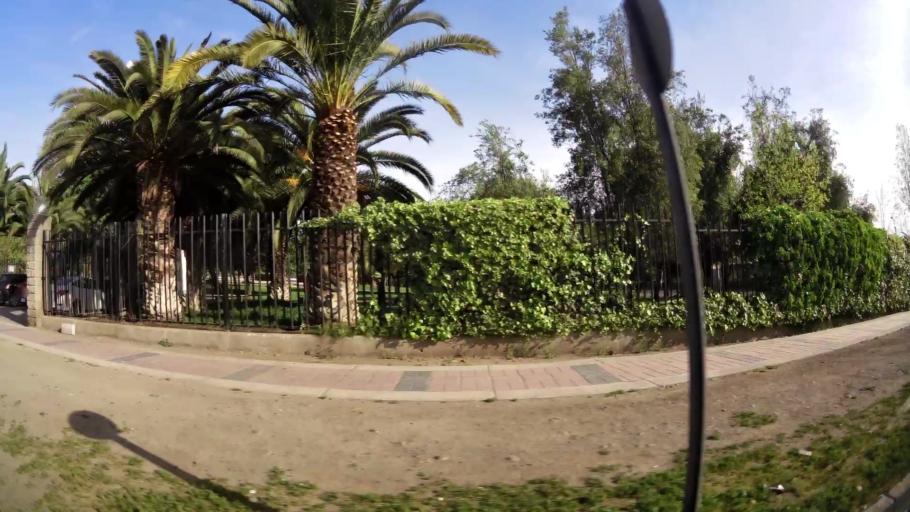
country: CL
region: Santiago Metropolitan
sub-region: Provincia de Santiago
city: Santiago
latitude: -33.5124
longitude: -70.6291
